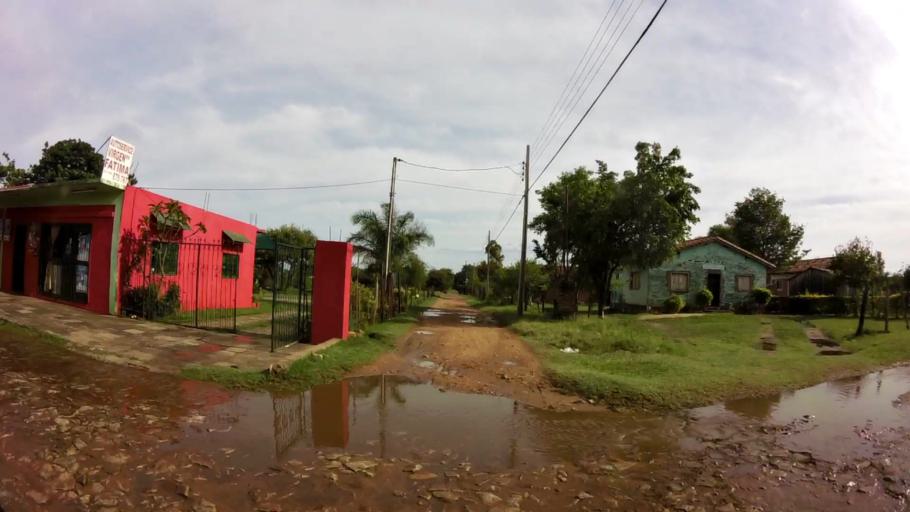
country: PY
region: Central
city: Limpio
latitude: -25.1674
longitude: -57.4882
